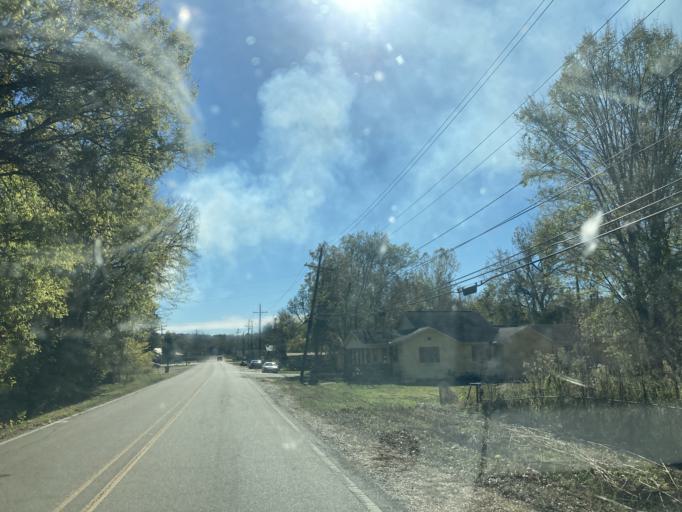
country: US
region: Mississippi
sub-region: Yazoo County
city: Yazoo City
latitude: 32.8558
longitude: -90.4112
